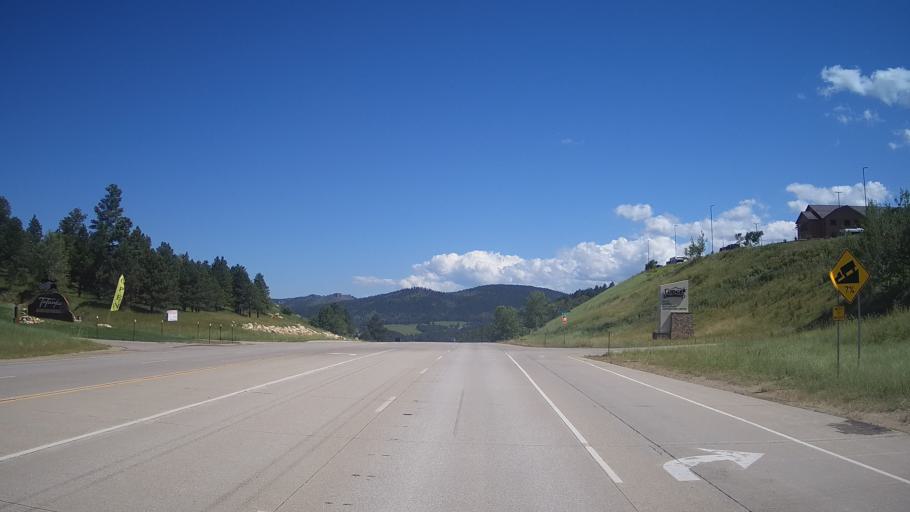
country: US
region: South Dakota
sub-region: Lawrence County
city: Deadwood
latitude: 44.3968
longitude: -103.7157
